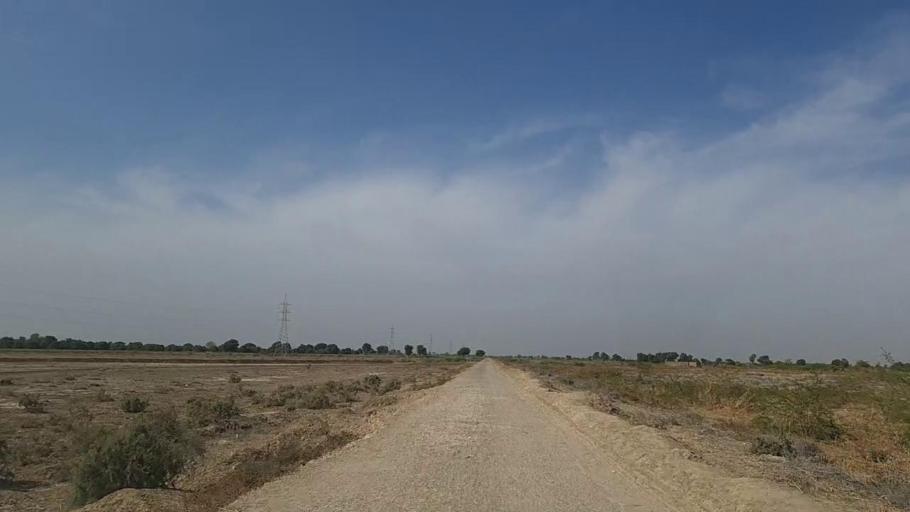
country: PK
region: Sindh
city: Samaro
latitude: 25.2115
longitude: 69.4550
